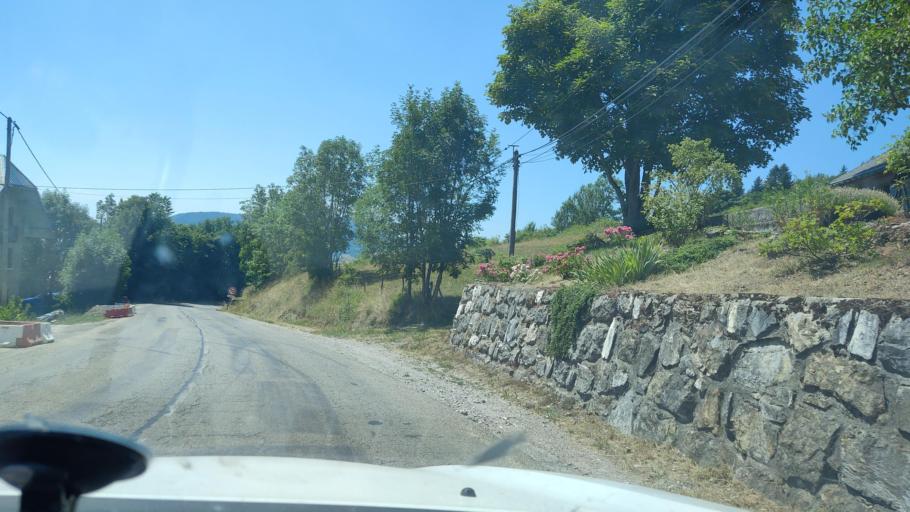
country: FR
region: Rhone-Alpes
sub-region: Departement de la Savoie
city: Mery
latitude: 45.6415
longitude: 6.0133
